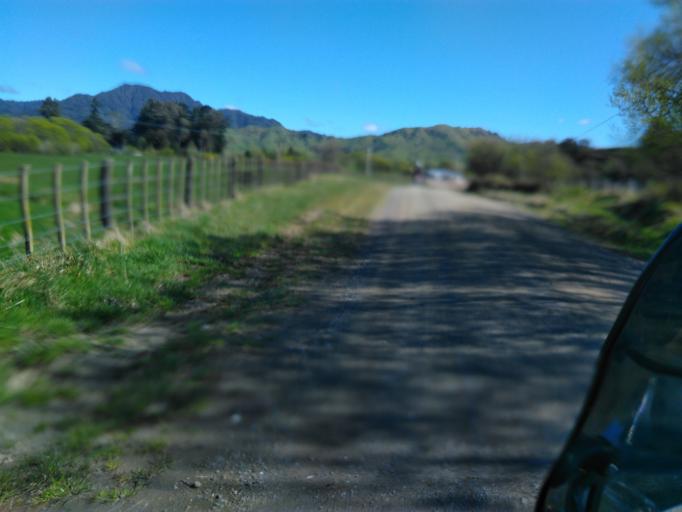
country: NZ
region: Bay of Plenty
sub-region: Opotiki District
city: Opotiki
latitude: -38.2833
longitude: 177.5417
